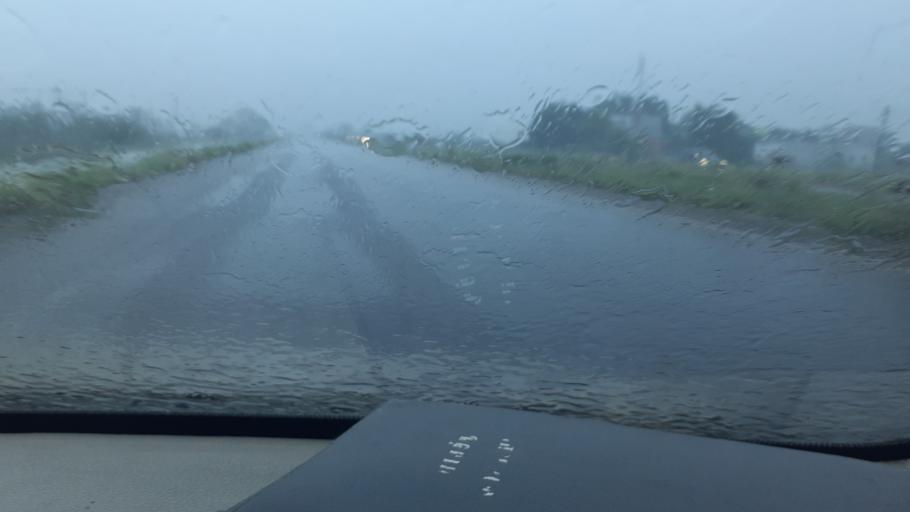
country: IN
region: Tamil Nadu
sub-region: Virudhunagar
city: Sattur
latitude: 9.4463
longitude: 77.9271
